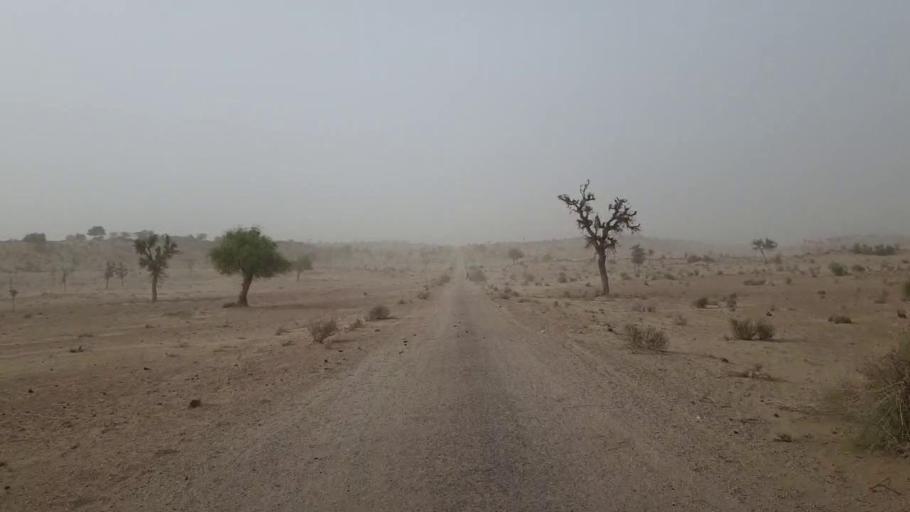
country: PK
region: Sindh
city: Islamkot
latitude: 24.5520
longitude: 70.3604
